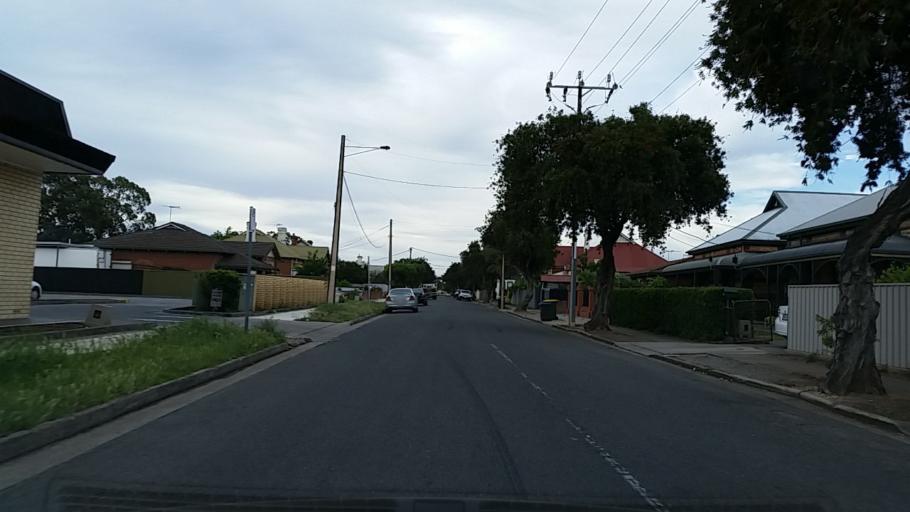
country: AU
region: South Australia
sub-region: Charles Sturt
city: Allenby Gardens
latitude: -34.9038
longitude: 138.5607
